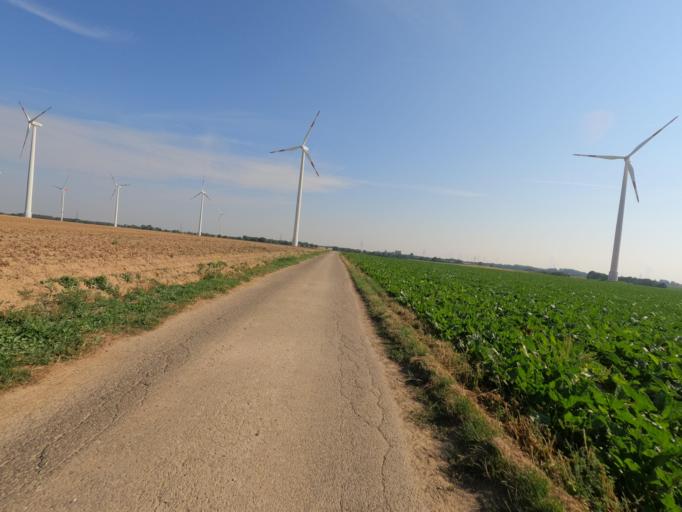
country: DE
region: North Rhine-Westphalia
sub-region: Regierungsbezirk Koln
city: Aldenhoven
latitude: 50.9254
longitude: 6.2767
